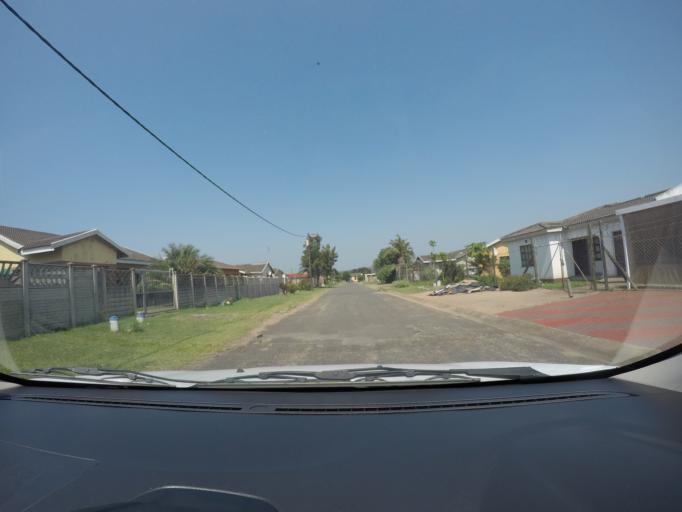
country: ZA
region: KwaZulu-Natal
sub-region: uThungulu District Municipality
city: eSikhawini
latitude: -28.8666
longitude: 31.9162
